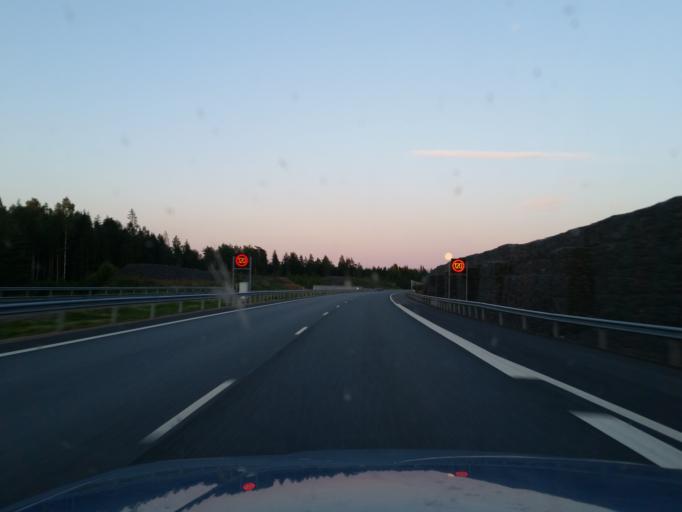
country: FI
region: Uusimaa
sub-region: Helsinki
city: Sammatti
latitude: 60.3669
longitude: 23.8705
